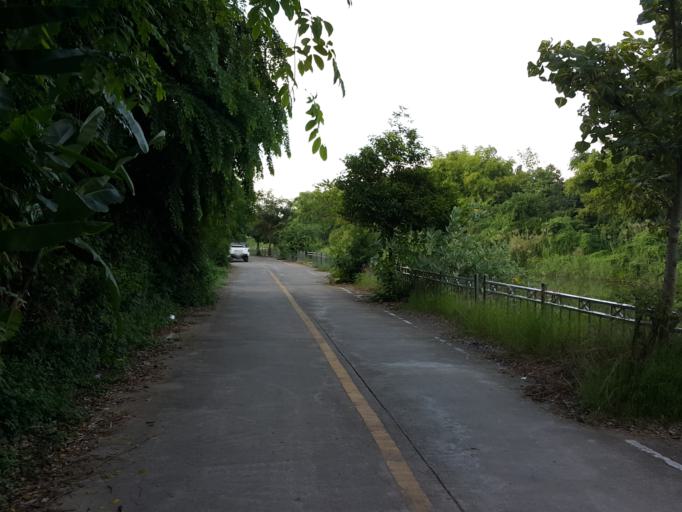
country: TH
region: Lampang
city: Lampang
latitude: 18.2965
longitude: 99.5126
